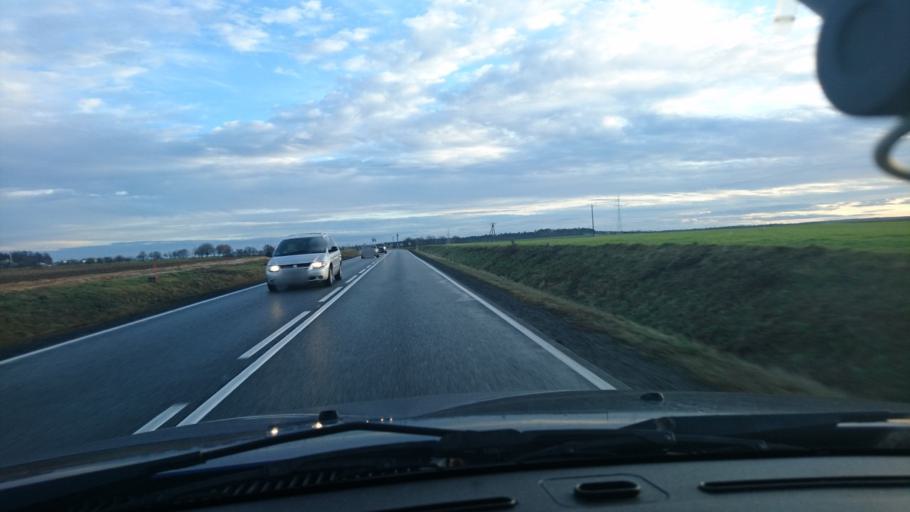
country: PL
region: Greater Poland Voivodeship
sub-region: Powiat kepinski
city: Baranow
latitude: 51.2477
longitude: 18.0173
